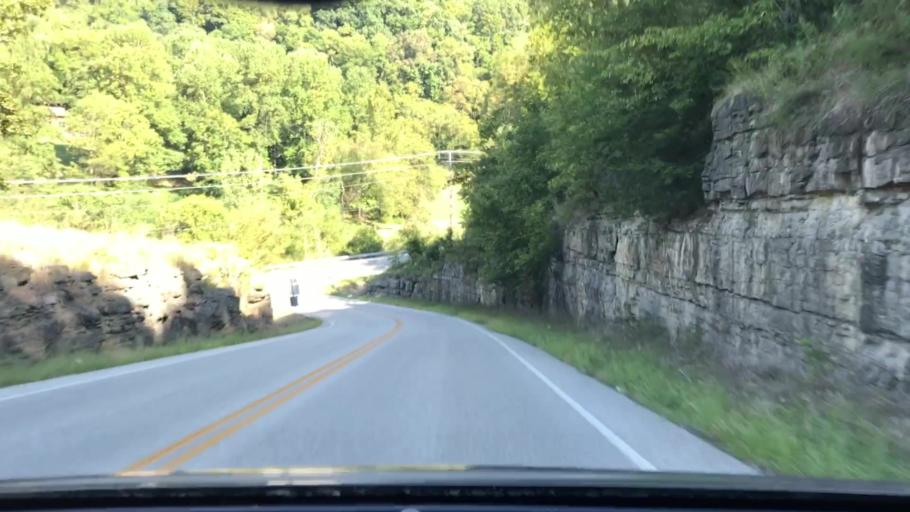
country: US
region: Tennessee
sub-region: Smith County
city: Carthage
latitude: 36.3208
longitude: -85.9418
